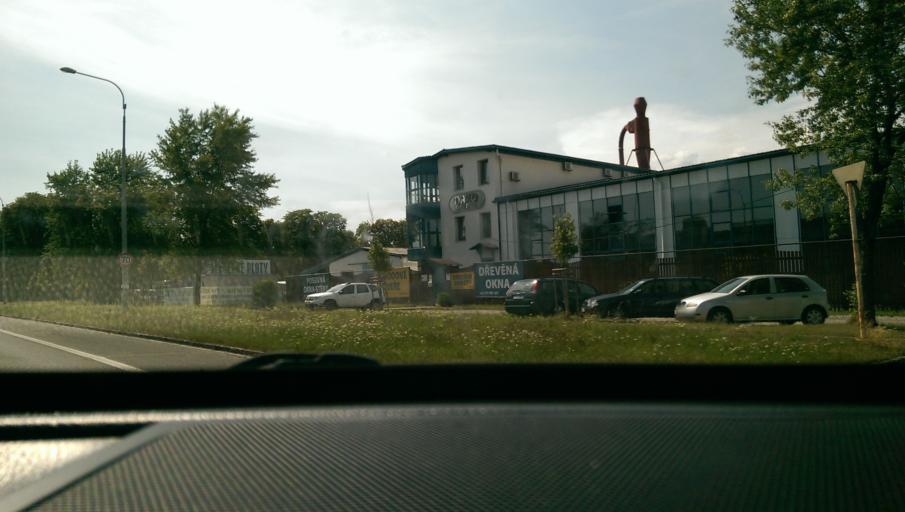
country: CZ
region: Moravskoslezsky
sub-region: Okres Ostrava-Mesto
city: Ostrava
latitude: 49.8579
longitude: 18.2616
